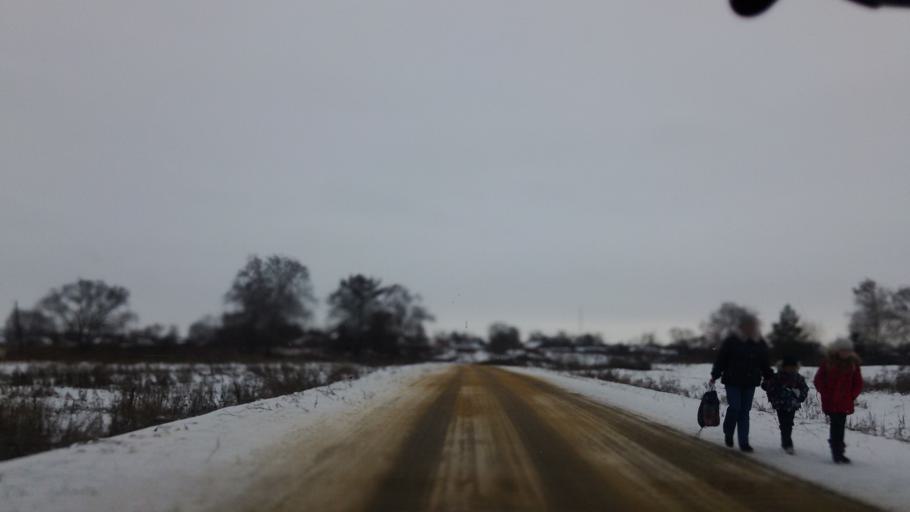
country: RU
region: Tula
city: Bogoroditsk
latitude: 53.7652
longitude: 37.9802
